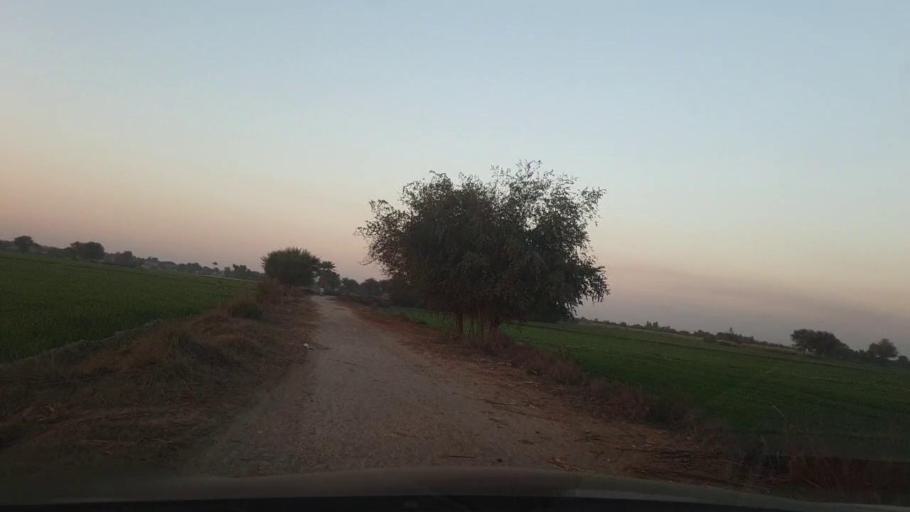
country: PK
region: Sindh
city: Ubauro
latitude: 28.1692
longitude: 69.6355
